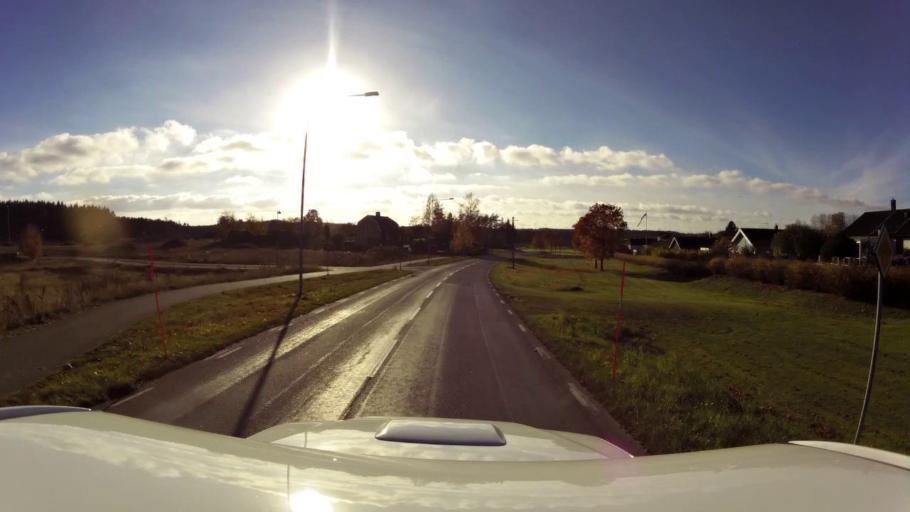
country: SE
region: OEstergoetland
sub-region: Linkopings Kommun
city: Vikingstad
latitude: 58.2873
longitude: 15.4461
